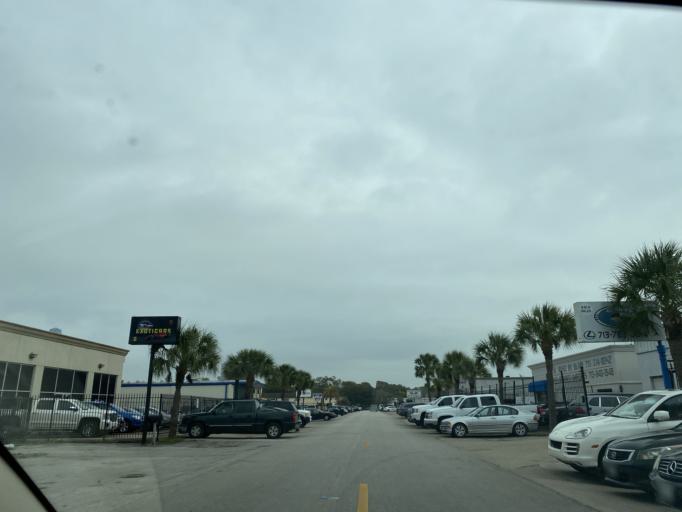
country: US
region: Texas
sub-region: Harris County
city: Bellaire
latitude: 29.7275
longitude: -95.4793
